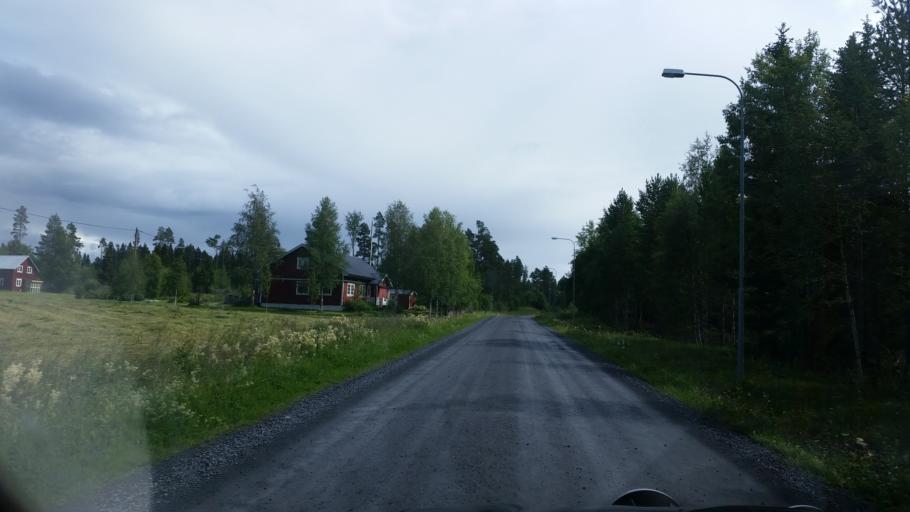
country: SE
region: Jaemtland
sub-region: Krokoms Kommun
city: Krokom
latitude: 63.3159
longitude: 14.3148
